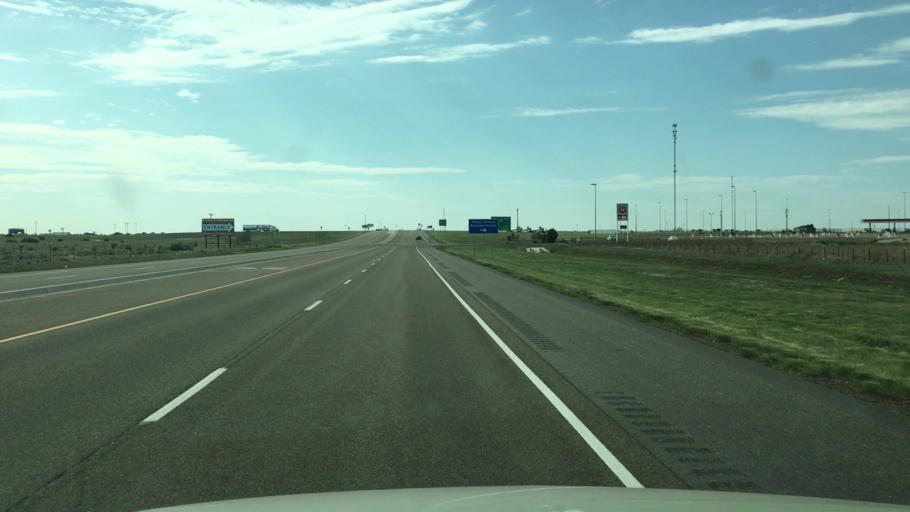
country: US
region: New Mexico
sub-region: Torrance County
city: Moriarty
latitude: 35.0137
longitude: -105.6673
